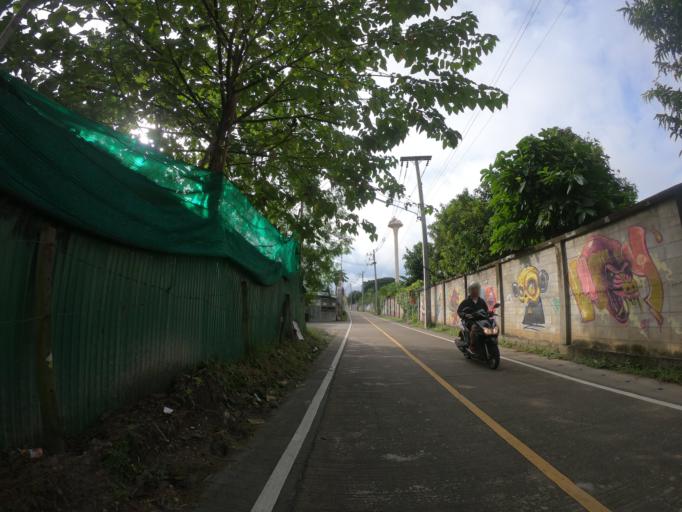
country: TH
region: Chiang Mai
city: Chiang Mai
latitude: 18.8176
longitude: 98.9646
